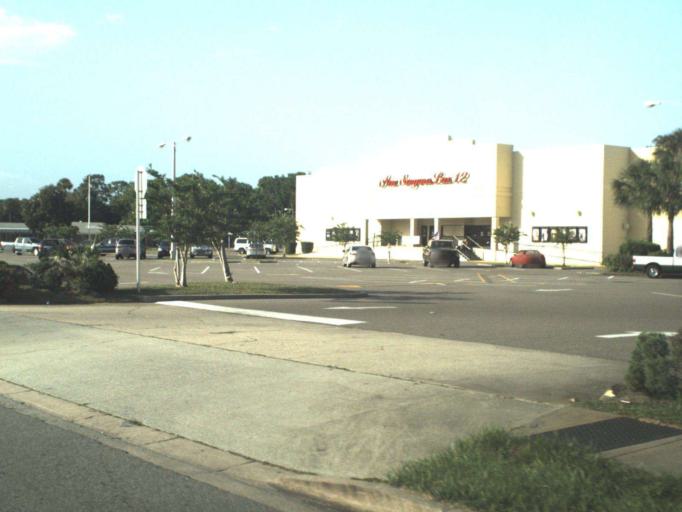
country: US
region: Florida
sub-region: Volusia County
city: New Smyrna Beach
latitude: 29.0088
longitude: -80.9195
